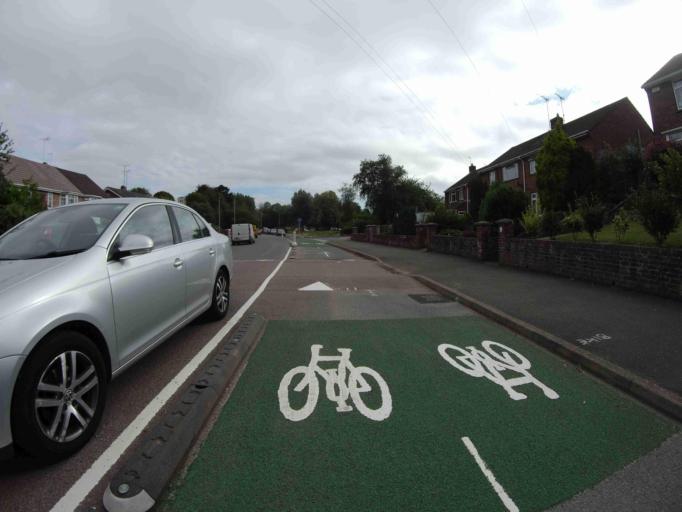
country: GB
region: England
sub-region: Devon
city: Heavitree
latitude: 50.7212
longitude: -3.4920
